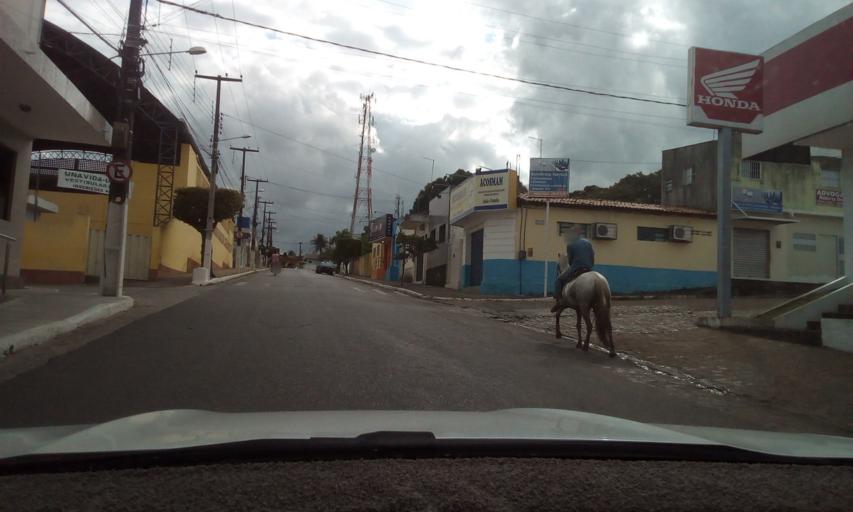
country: BR
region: Paraiba
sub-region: Mamanguape
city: Mamanguape
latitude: -6.8356
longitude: -35.1236
